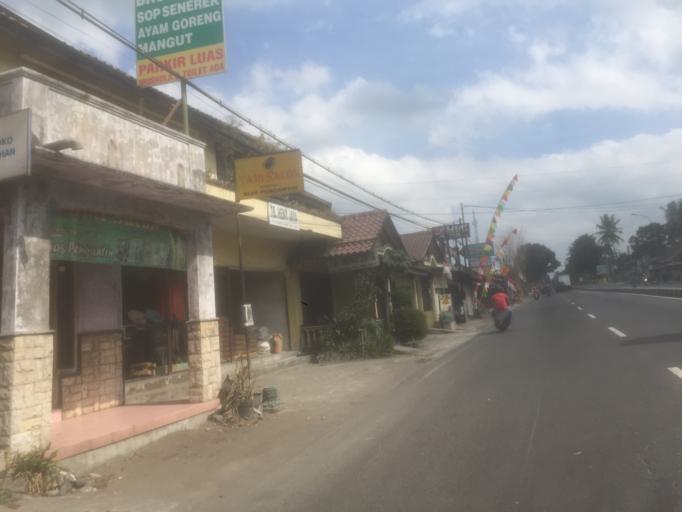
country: ID
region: Daerah Istimewa Yogyakarta
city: Sleman
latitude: -7.6682
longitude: 110.3327
